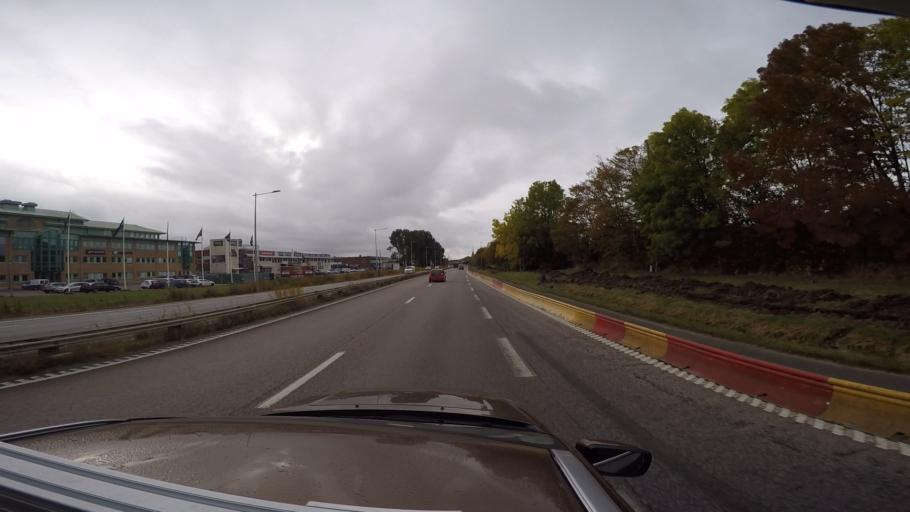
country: SE
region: Vaestra Goetaland
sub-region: Goteborg
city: Majorna
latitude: 57.6553
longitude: 11.9344
